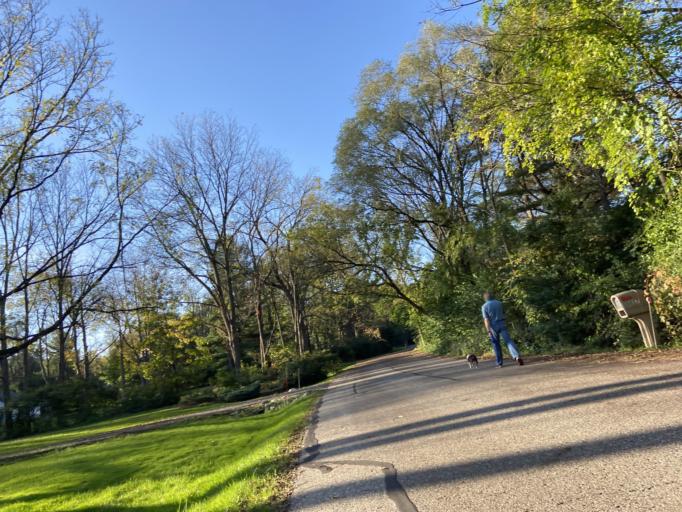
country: US
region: Michigan
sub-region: Oakland County
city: Franklin
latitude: 42.5101
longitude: -83.3321
